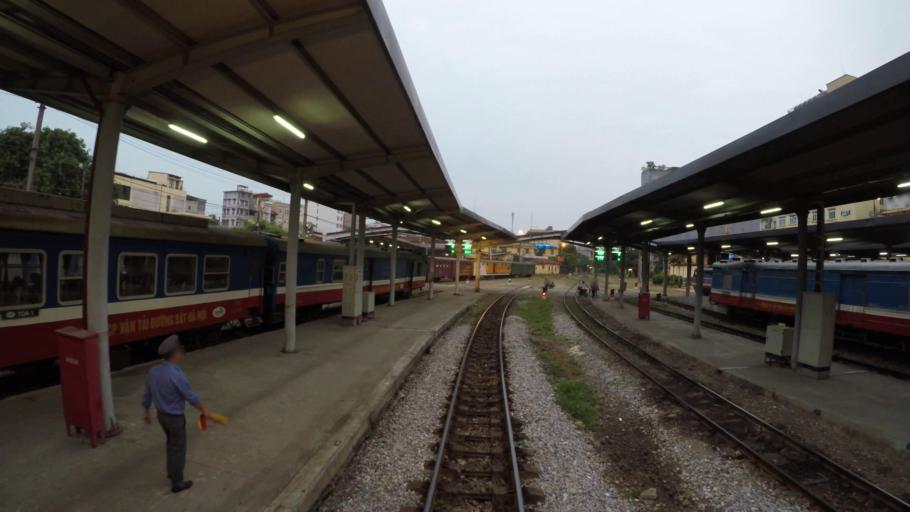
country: VN
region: Ha Noi
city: Hanoi
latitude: 21.0267
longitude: 105.8411
